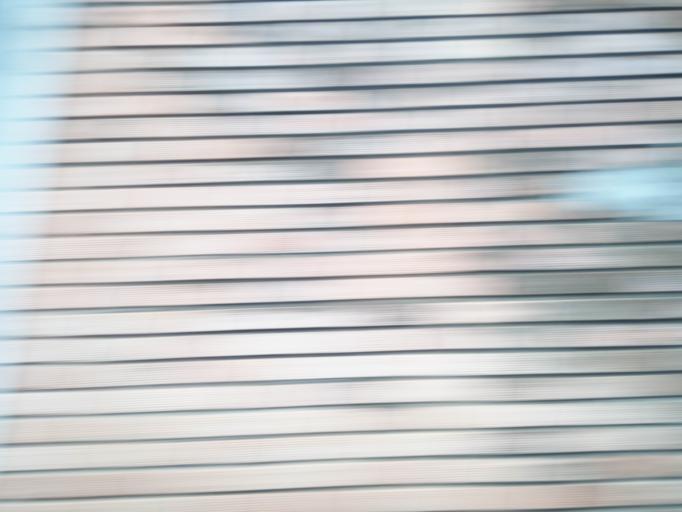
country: TH
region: Phuket
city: Ban Talat Nua
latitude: 7.8775
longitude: 98.3801
